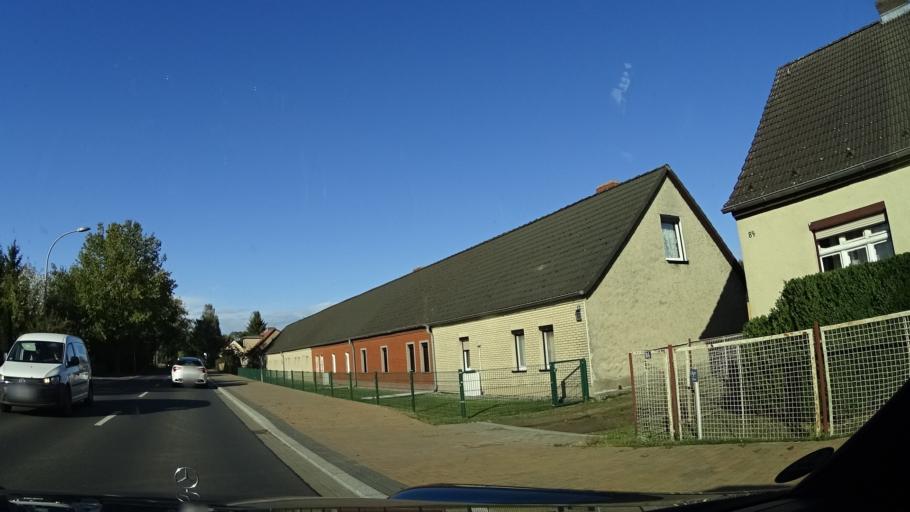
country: DE
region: Brandenburg
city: Neuruppin
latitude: 52.8963
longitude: 12.7987
